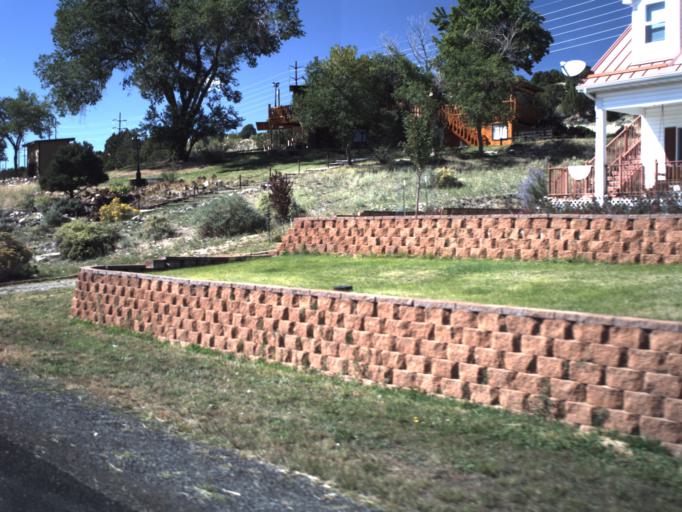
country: US
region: Utah
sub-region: Beaver County
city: Beaver
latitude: 38.2816
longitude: -112.5991
